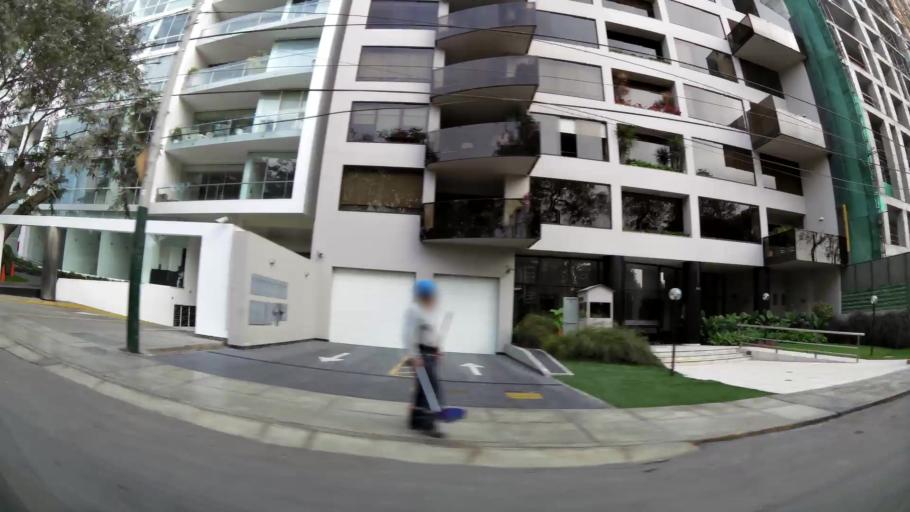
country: PE
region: Lima
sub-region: Lima
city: San Isidro
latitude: -12.1024
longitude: -77.0438
